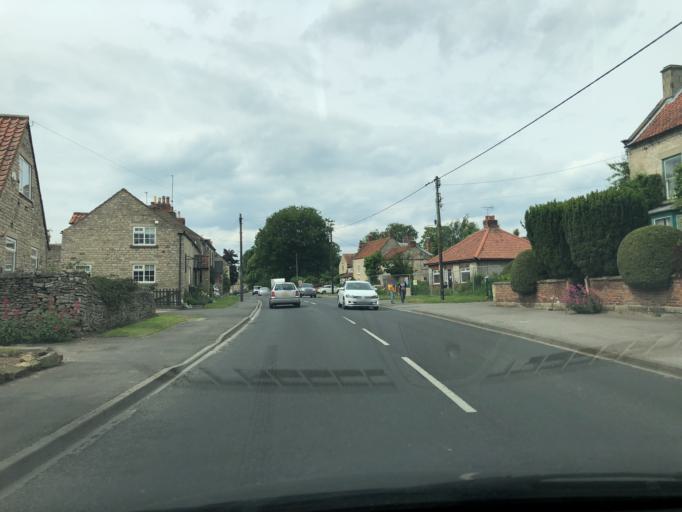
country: GB
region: England
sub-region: North Yorkshire
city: Pickering
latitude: 54.2568
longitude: -0.7988
